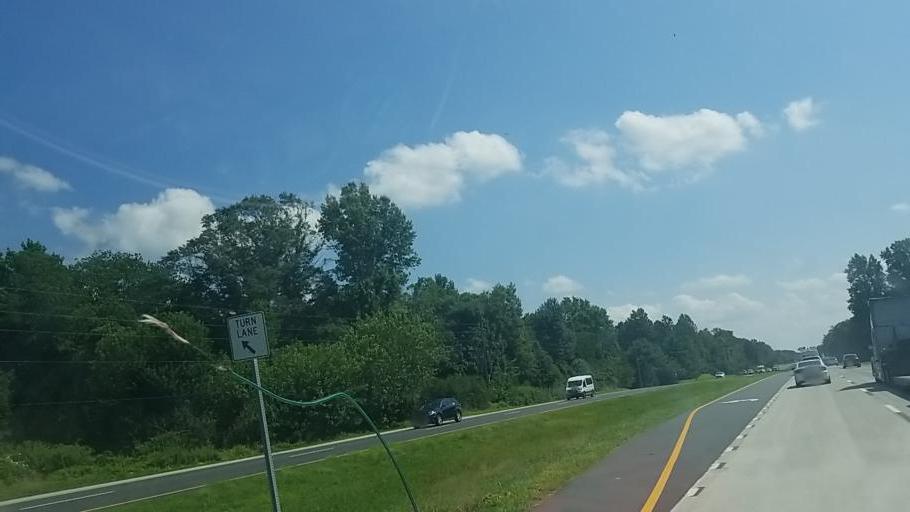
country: US
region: Delaware
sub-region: Sussex County
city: Milford
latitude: 38.8416
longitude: -75.4392
